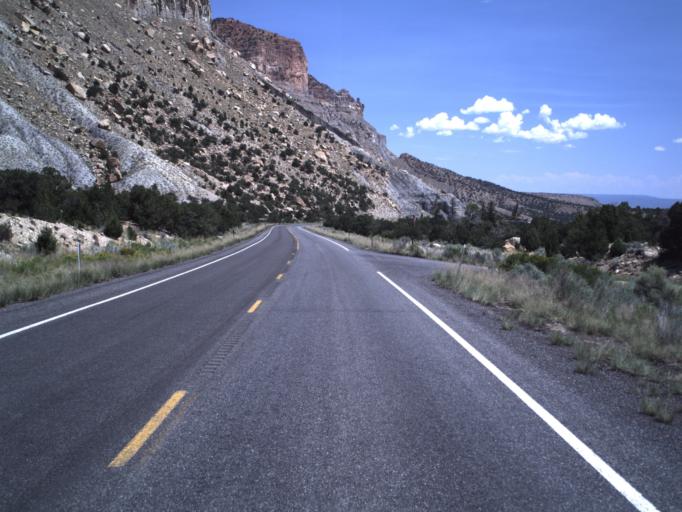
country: US
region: Utah
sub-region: Emery County
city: Huntington
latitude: 39.3933
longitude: -111.0997
